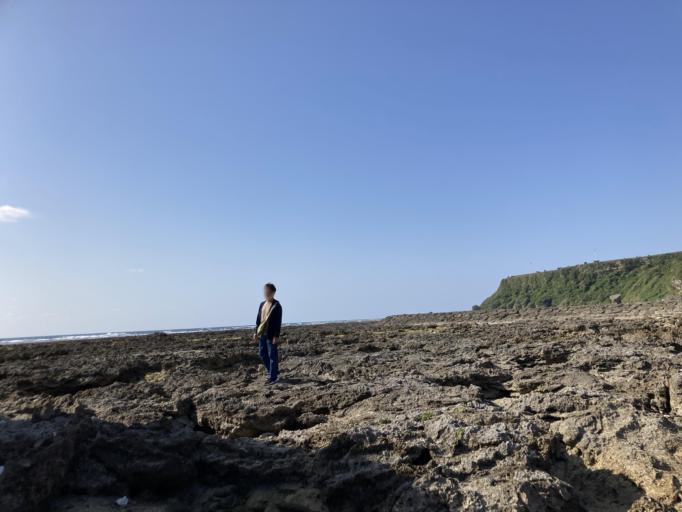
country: JP
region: Okinawa
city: Itoman
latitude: 26.1171
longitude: 127.7465
